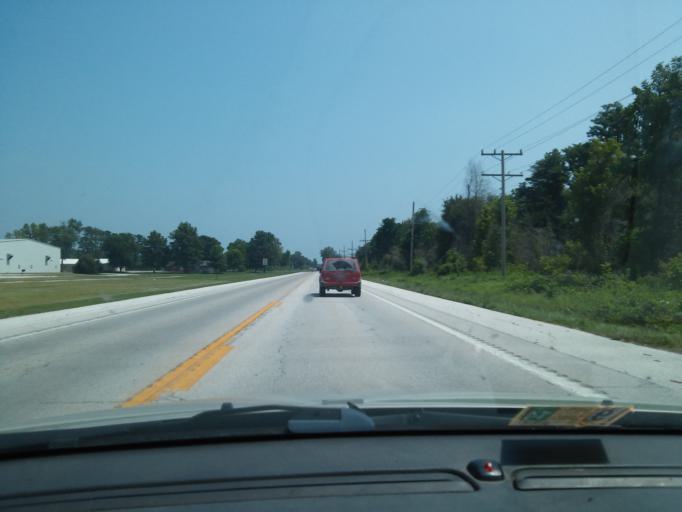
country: US
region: Missouri
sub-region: Pike County
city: Louisiana
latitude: 39.4142
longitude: -91.0978
